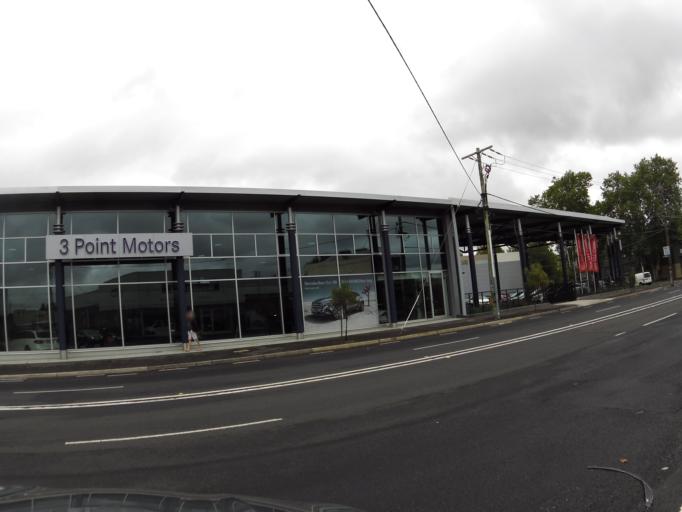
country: AU
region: Victoria
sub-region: Darebin
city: Fairfield
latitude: -37.7828
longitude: 145.0194
